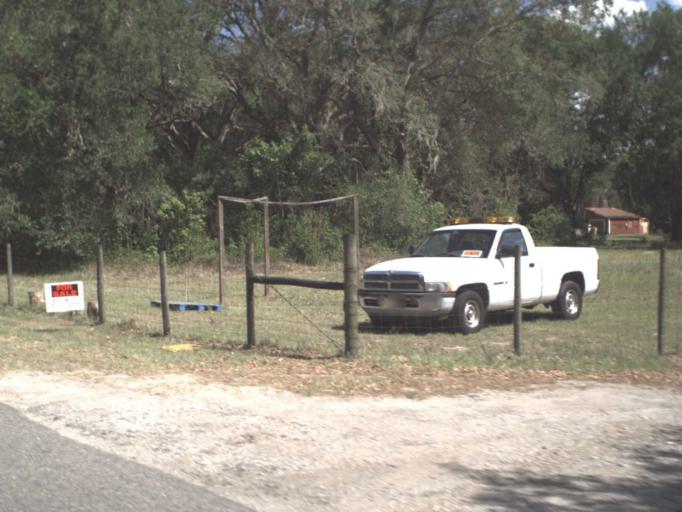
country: US
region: Florida
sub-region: Lake County
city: Mount Plymouth
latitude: 28.8184
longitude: -81.4801
